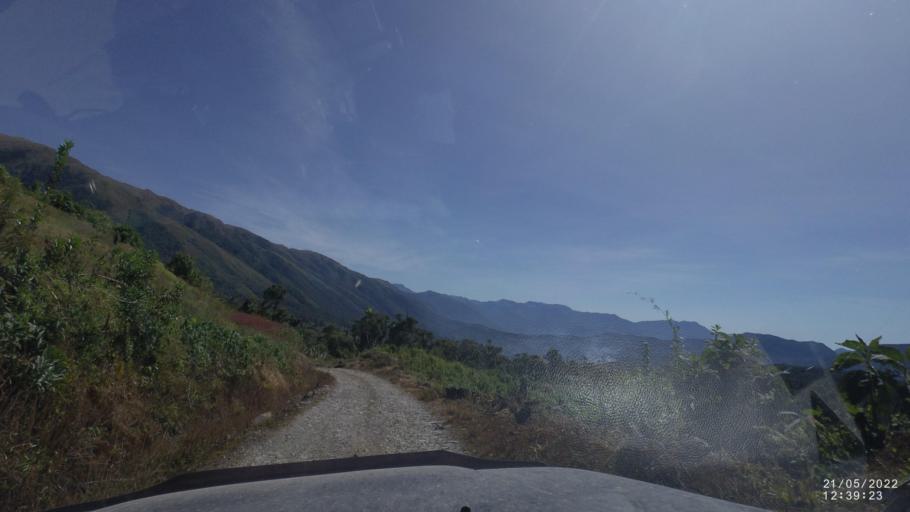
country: BO
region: Cochabamba
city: Colomi
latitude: -17.1977
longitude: -65.9225
